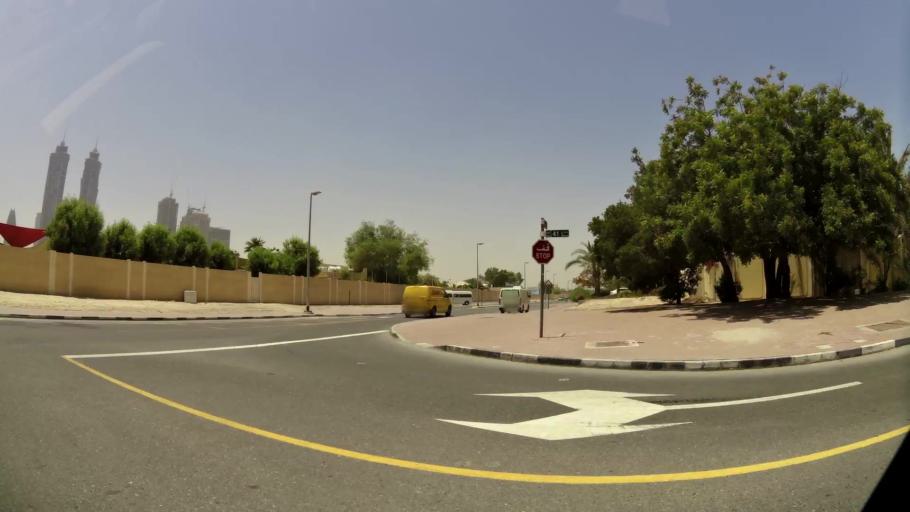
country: AE
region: Dubai
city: Dubai
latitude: 25.1933
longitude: 55.2514
